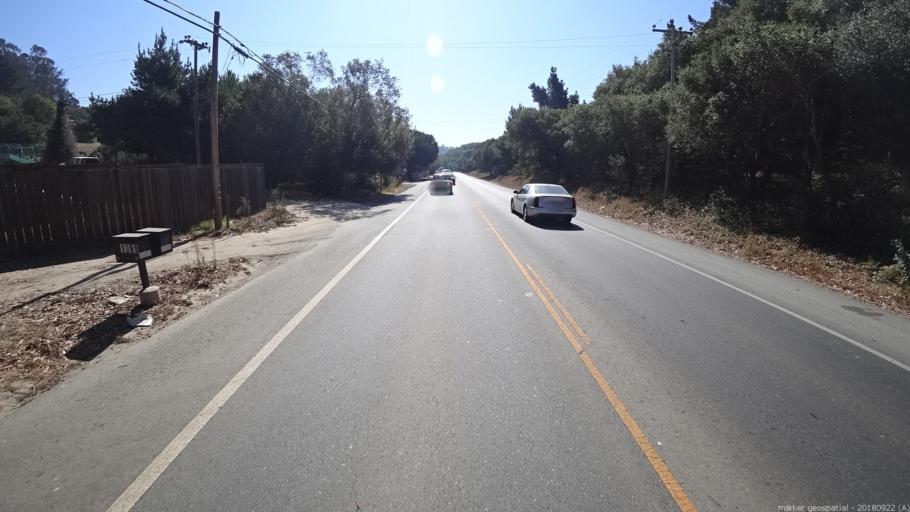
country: US
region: California
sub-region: Monterey County
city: Las Lomas
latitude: 36.8424
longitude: -121.6885
